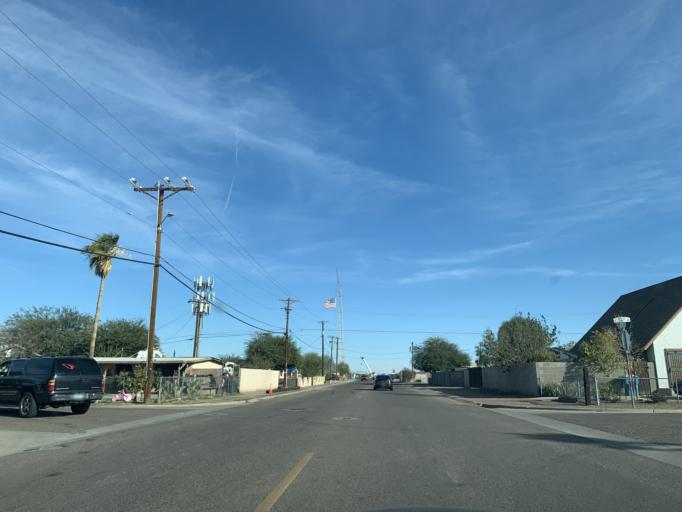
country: US
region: Arizona
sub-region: Maricopa County
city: Laveen
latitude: 33.4029
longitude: -112.1358
